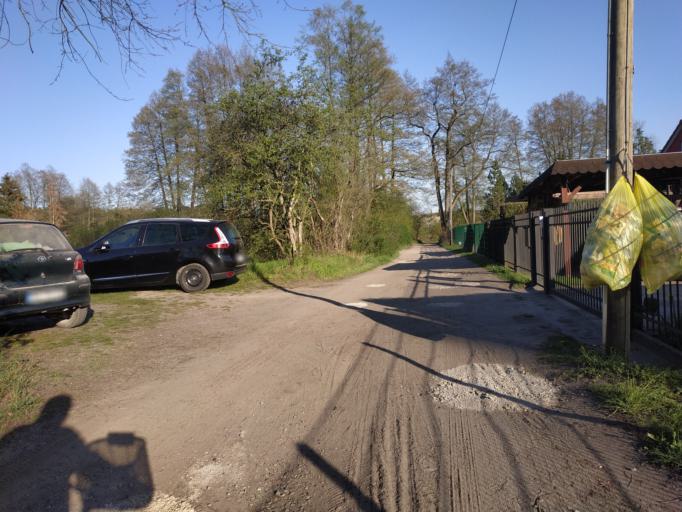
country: DE
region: Brandenburg
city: Strausberg
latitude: 52.5591
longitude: 13.8442
